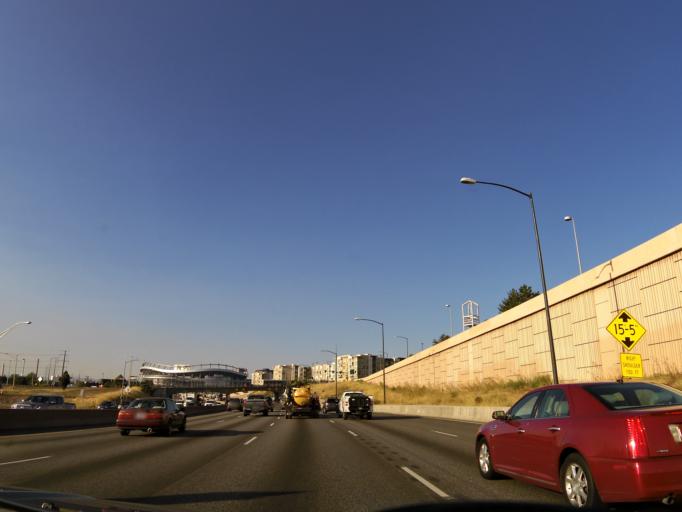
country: US
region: Colorado
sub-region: Denver County
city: Denver
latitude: 39.7530
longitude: -105.0157
